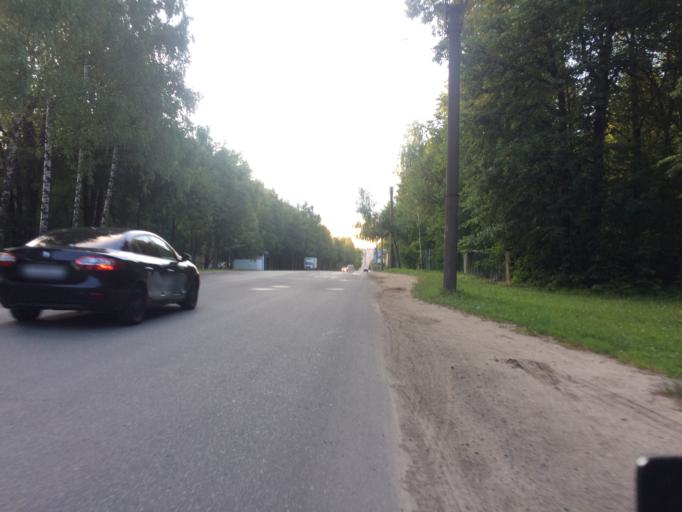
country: RU
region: Mariy-El
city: Yoshkar-Ola
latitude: 56.6250
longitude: 47.9538
